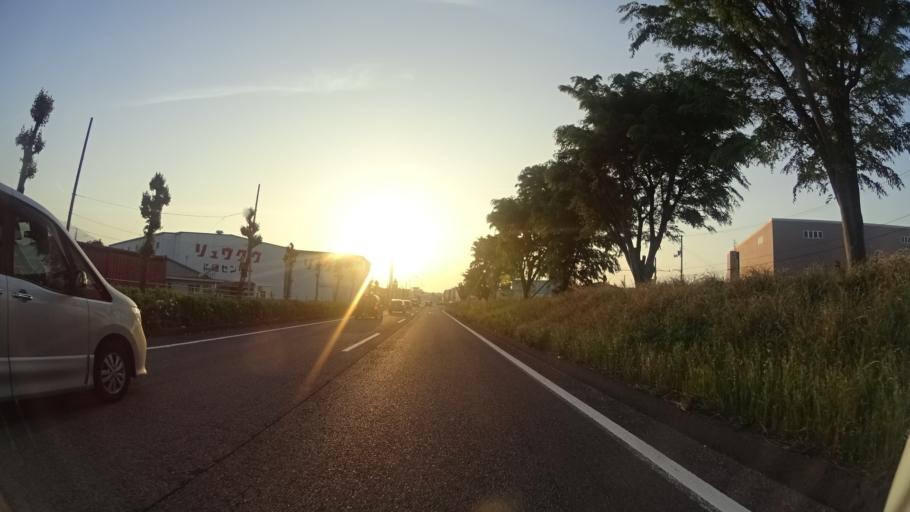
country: JP
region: Ehime
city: Kawanoecho
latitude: 33.9859
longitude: 133.5703
